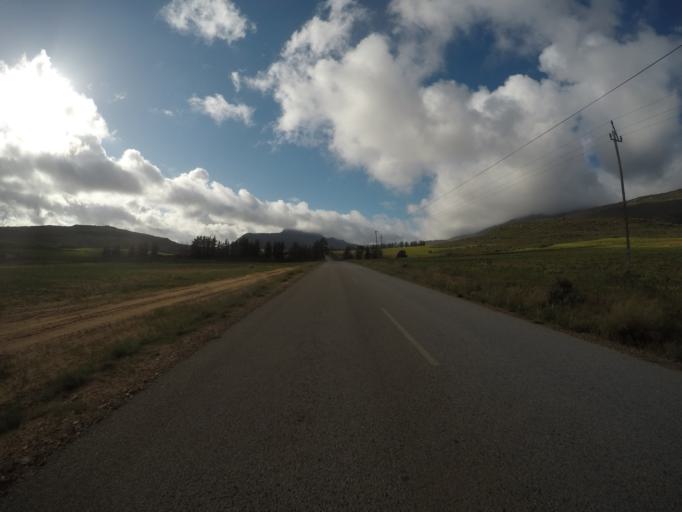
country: ZA
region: Western Cape
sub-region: West Coast District Municipality
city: Clanwilliam
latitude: -32.3454
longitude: 18.8413
